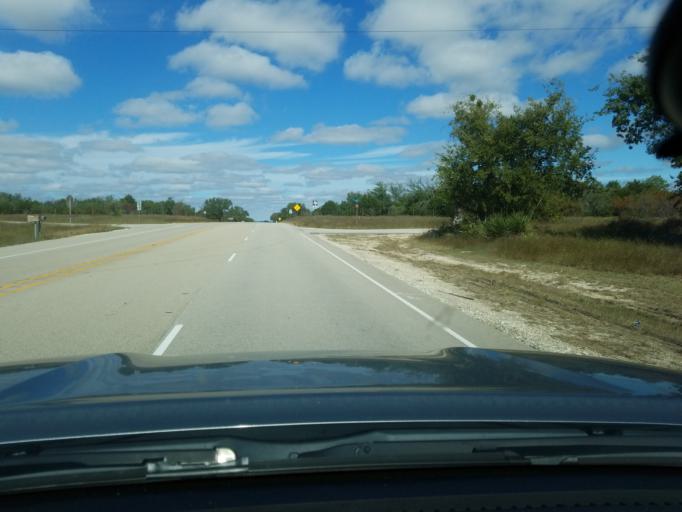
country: US
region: Texas
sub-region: Hamilton County
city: Hamilton
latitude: 31.5923
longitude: -98.1569
